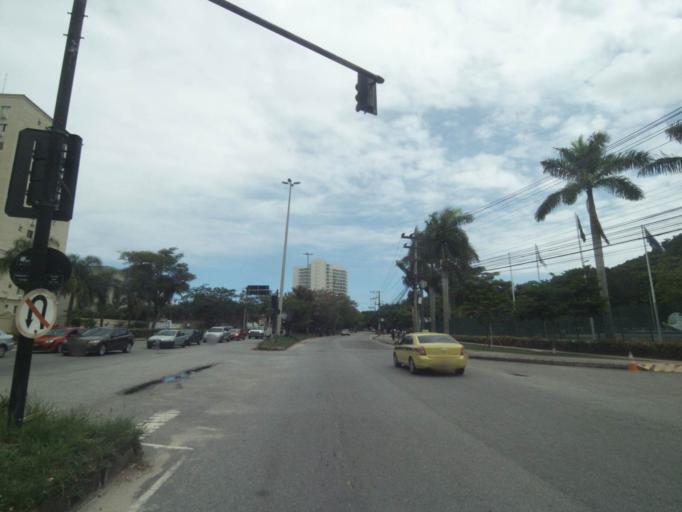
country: BR
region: Rio de Janeiro
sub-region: Nilopolis
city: Nilopolis
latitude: -22.9728
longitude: -43.4142
